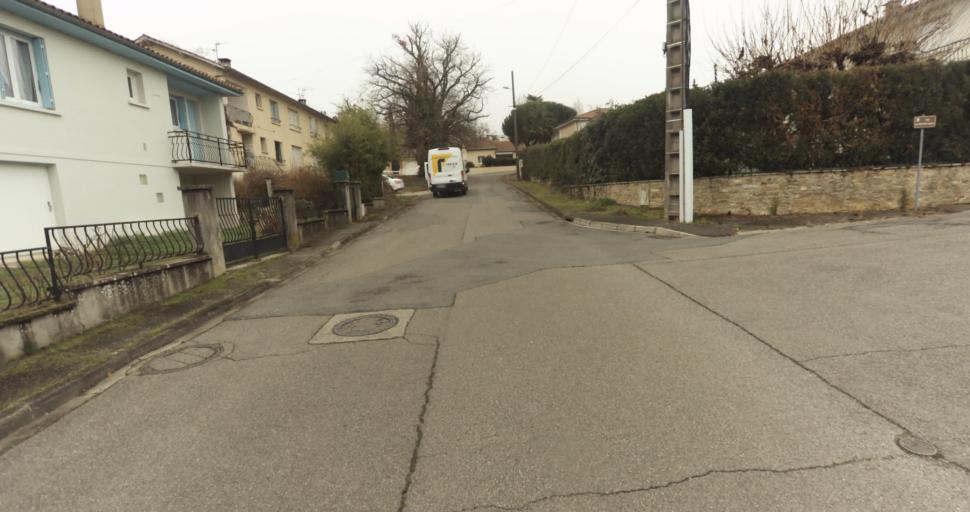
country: FR
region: Midi-Pyrenees
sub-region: Departement du Lot
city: Figeac
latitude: 44.6103
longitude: 2.0405
